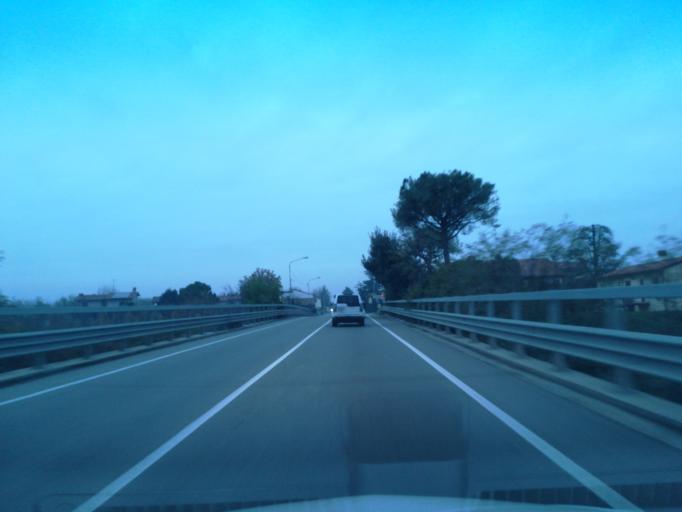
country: IT
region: Emilia-Romagna
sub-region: Provincia di Ravenna
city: Castel Bolognese
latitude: 44.3100
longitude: 11.8248
